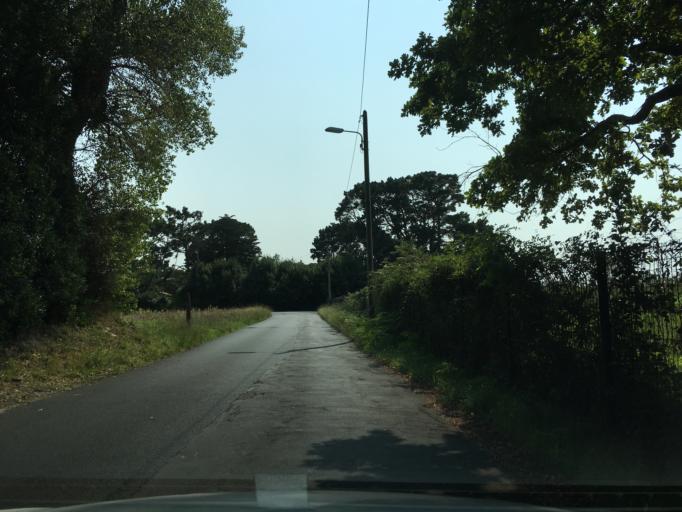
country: FR
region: Aquitaine
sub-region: Departement des Pyrenees-Atlantiques
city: Anglet
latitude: 43.5011
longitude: -1.5211
